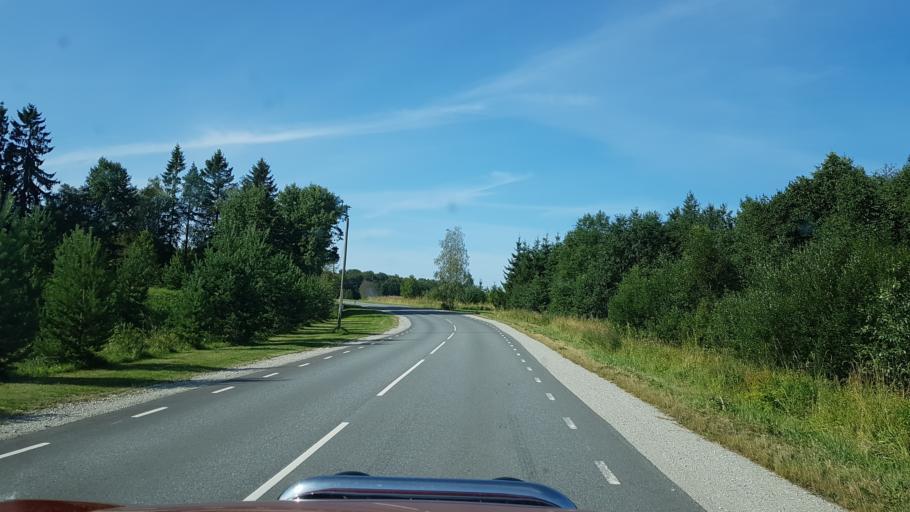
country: EE
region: Harju
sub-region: Rae vald
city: Jueri
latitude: 59.3835
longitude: 24.9300
